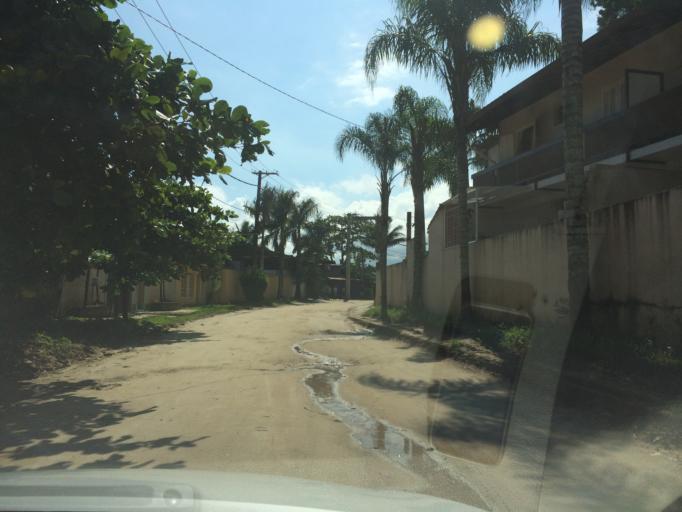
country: BR
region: Sao Paulo
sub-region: Biritiba-Mirim
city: Biritiba Mirim
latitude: -23.7632
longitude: -45.7600
